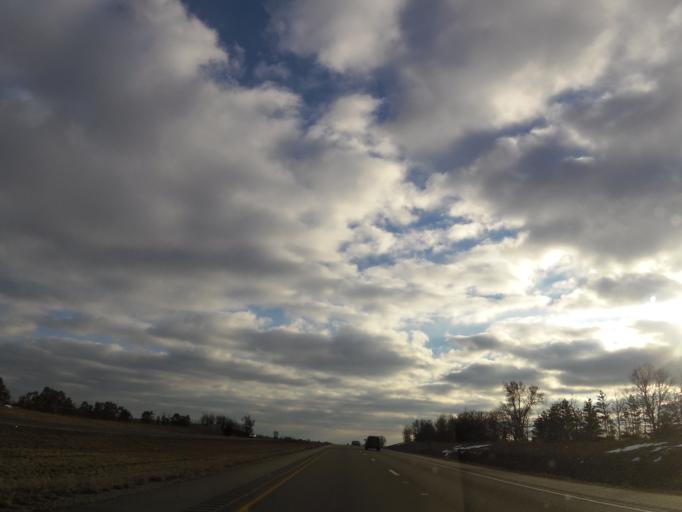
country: US
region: Illinois
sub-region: Ogle County
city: Davis Junction
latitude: 42.1470
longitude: -89.0236
